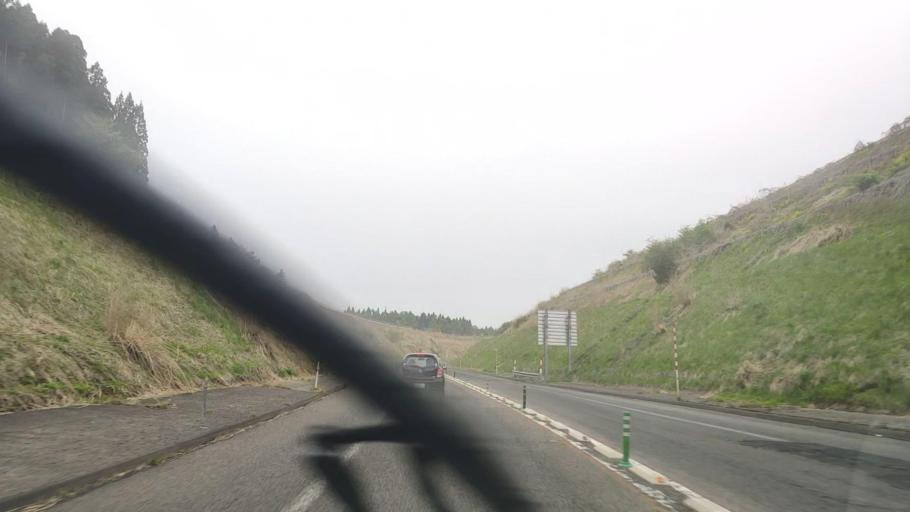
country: JP
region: Akita
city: Noshiromachi
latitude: 40.2106
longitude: 140.1939
